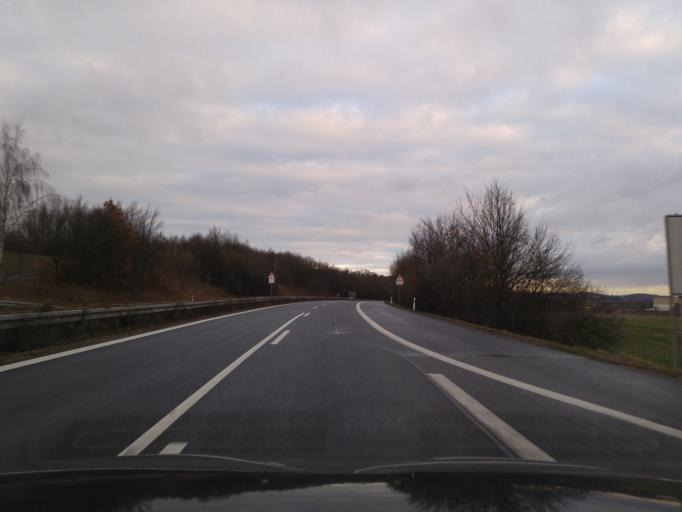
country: DE
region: Saxony
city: Dennheritz
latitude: 50.7916
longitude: 12.4777
